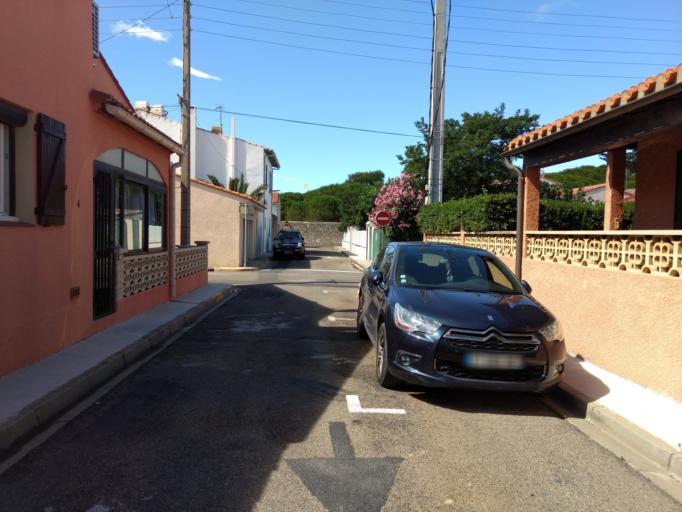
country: FR
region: Languedoc-Roussillon
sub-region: Departement des Pyrenees-Orientales
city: Le Barcares
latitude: 42.7856
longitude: 3.0357
